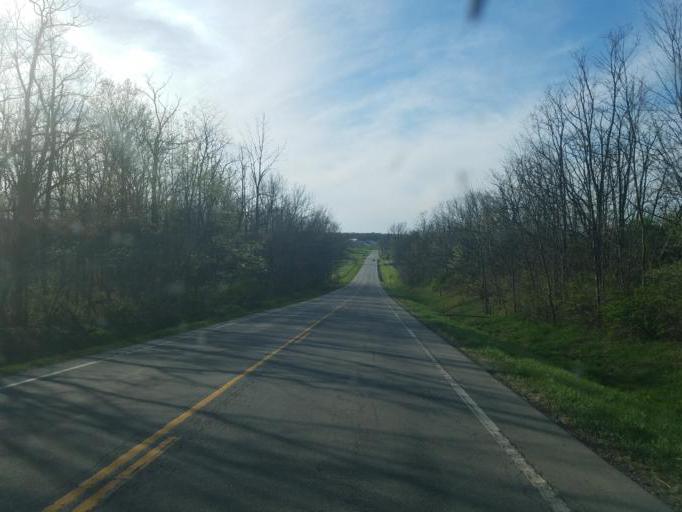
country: US
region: Ohio
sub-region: Huron County
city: New London
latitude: 41.0013
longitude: -82.3981
